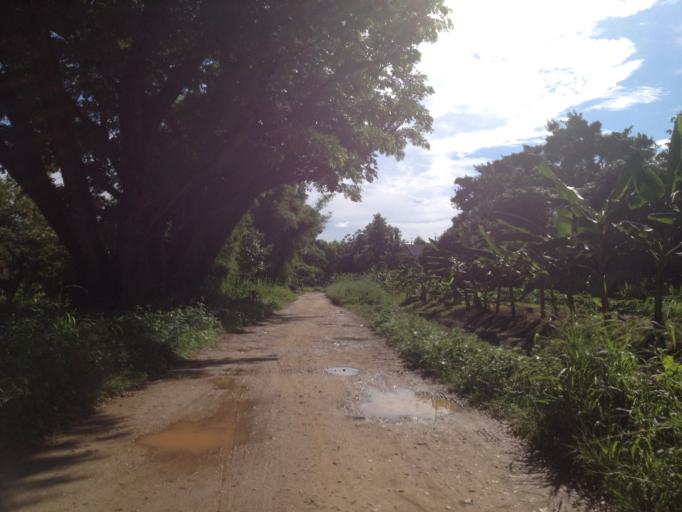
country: TH
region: Chiang Mai
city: Hang Dong
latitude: 18.6949
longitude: 98.9005
